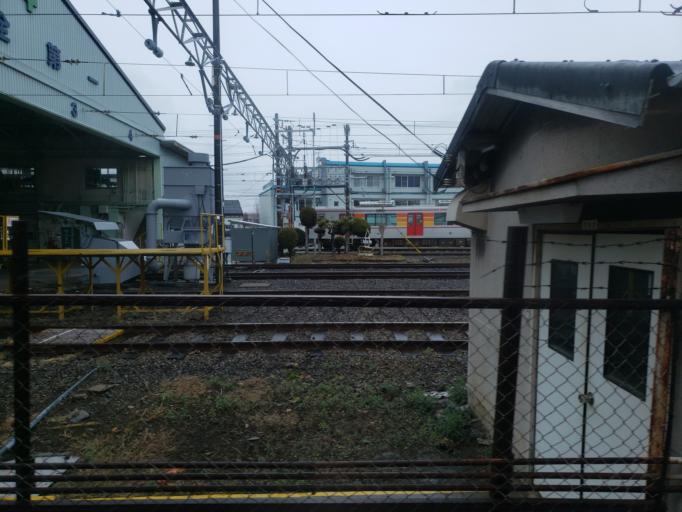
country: JP
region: Hyogo
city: Kakogawacho-honmachi
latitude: 34.7019
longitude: 134.8855
